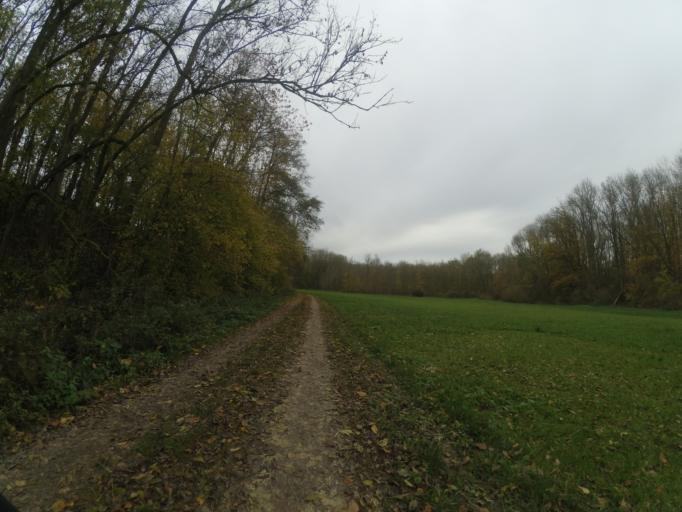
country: DE
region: Baden-Wuerttemberg
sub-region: Tuebingen Region
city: Staig
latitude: 48.3441
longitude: 10.0028
